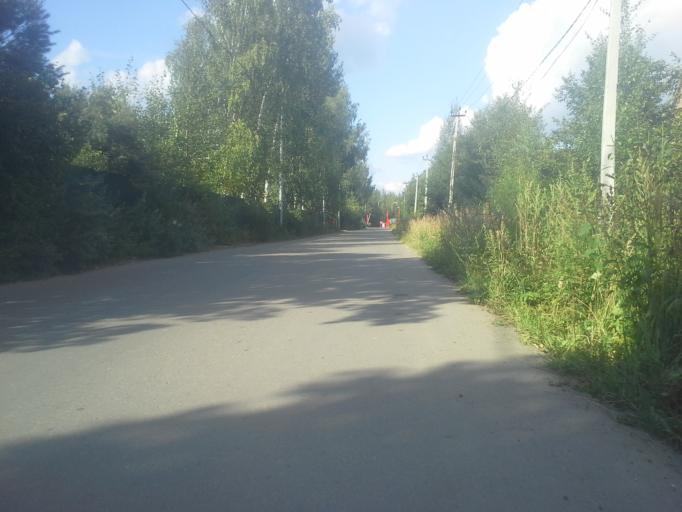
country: RU
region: Moskovskaya
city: Kievskij
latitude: 55.3523
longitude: 36.9504
